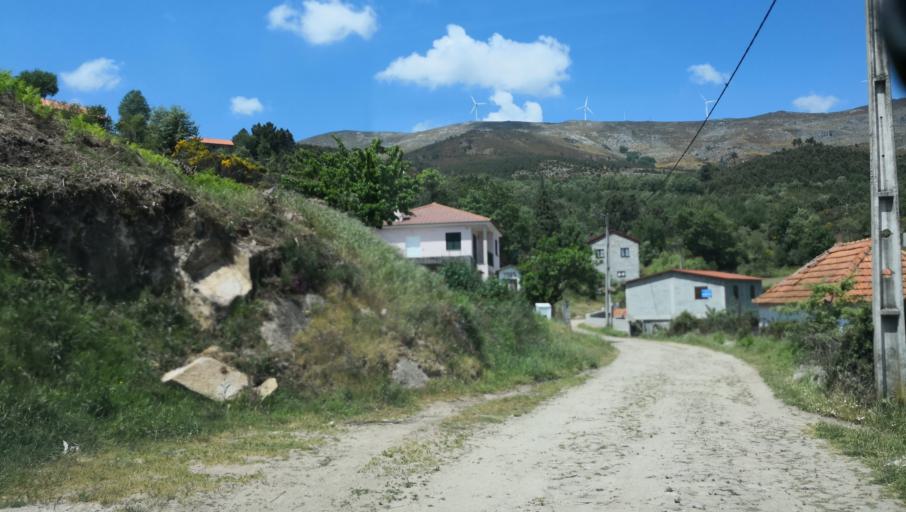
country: PT
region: Vila Real
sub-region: Vila Real
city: Vila Real
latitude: 41.3628
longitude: -7.7308
